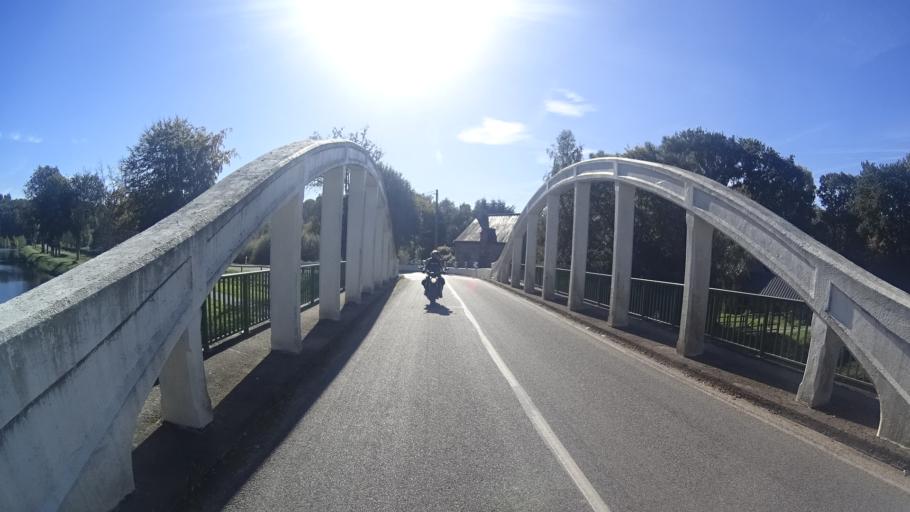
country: FR
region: Brittany
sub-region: Departement du Morbihan
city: Peillac
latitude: 47.7291
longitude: -2.2144
